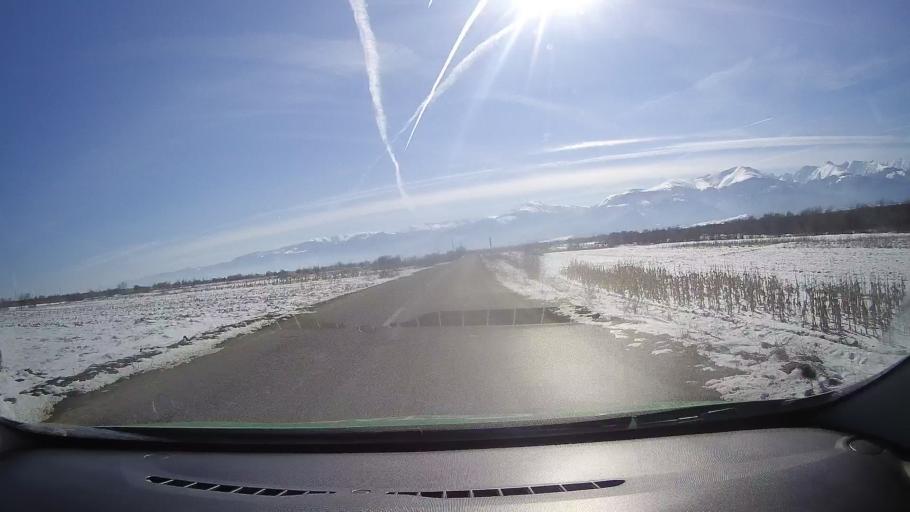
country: RO
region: Brasov
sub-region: Comuna Sambata de Sus
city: Sambata de Sus
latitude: 45.7535
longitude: 24.8347
